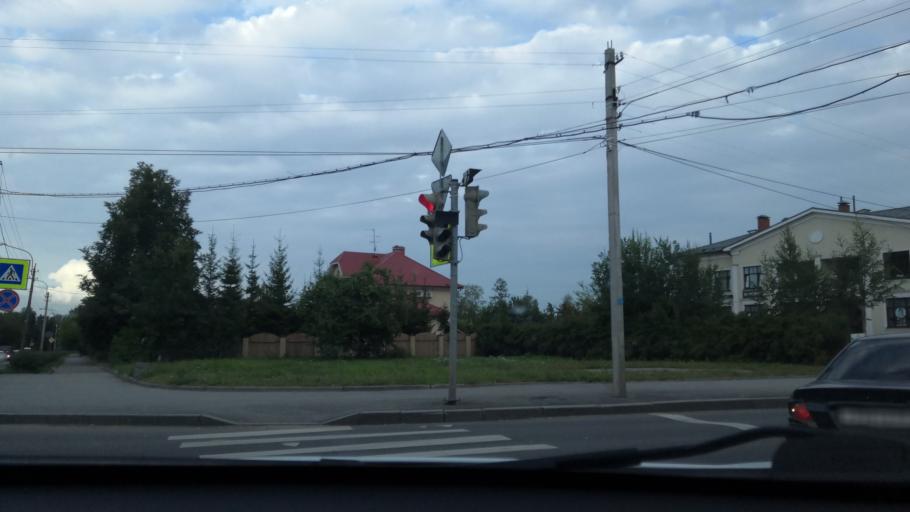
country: RU
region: St.-Petersburg
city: Pushkin
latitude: 59.7028
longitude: 30.4073
